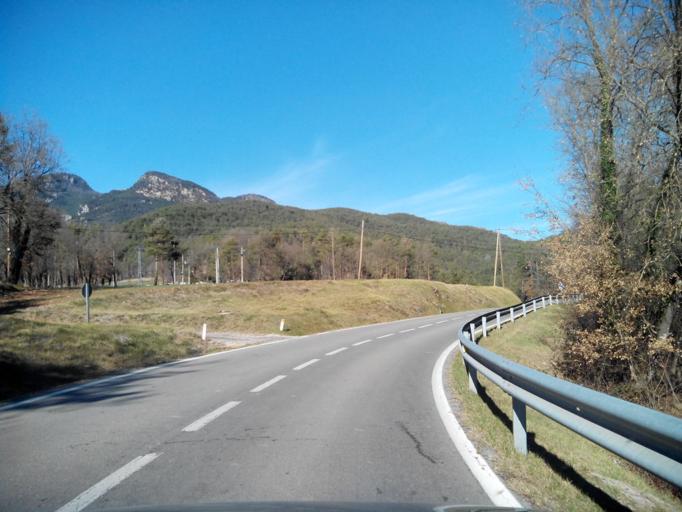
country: ES
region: Catalonia
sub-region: Provincia de Barcelona
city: Vilada
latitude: 42.1335
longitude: 1.9191
